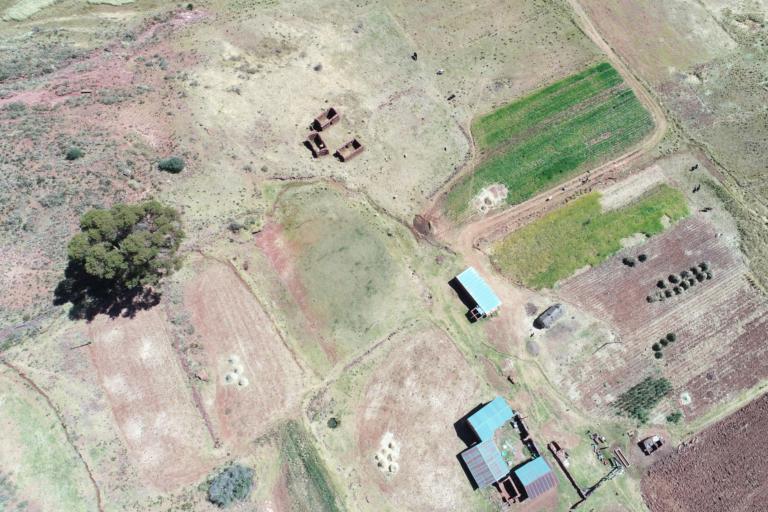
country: BO
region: La Paz
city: Tiahuanaco
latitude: -16.6031
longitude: -68.7717
